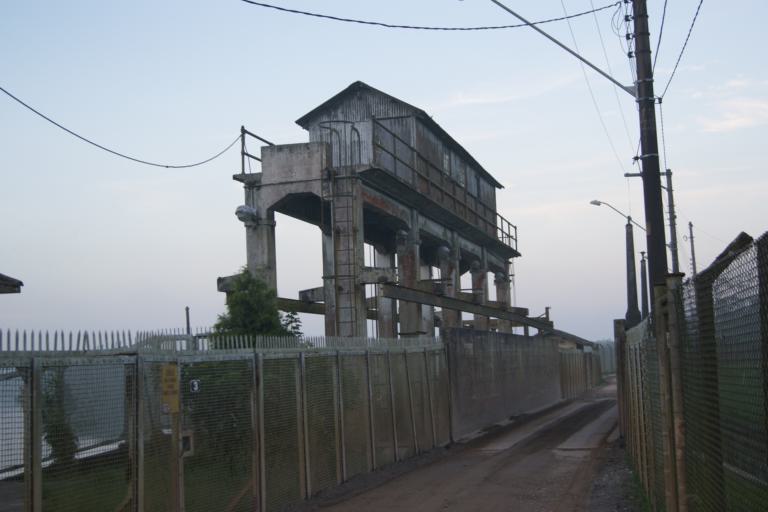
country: BR
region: Sao Paulo
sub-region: Cubatao
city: Cubatao
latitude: -23.8115
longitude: -46.4619
